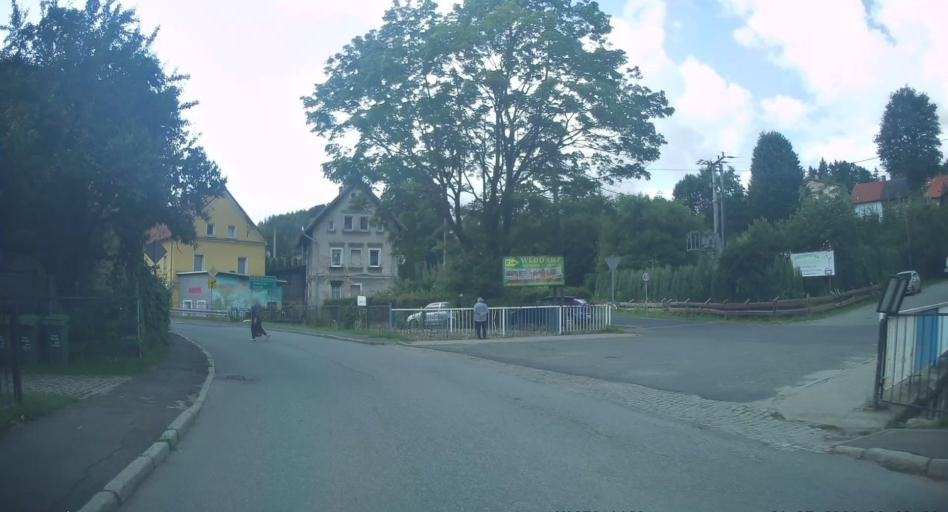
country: PL
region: Lower Silesian Voivodeship
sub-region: Powiat walbrzyski
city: Walim
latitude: 50.6979
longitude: 16.4416
